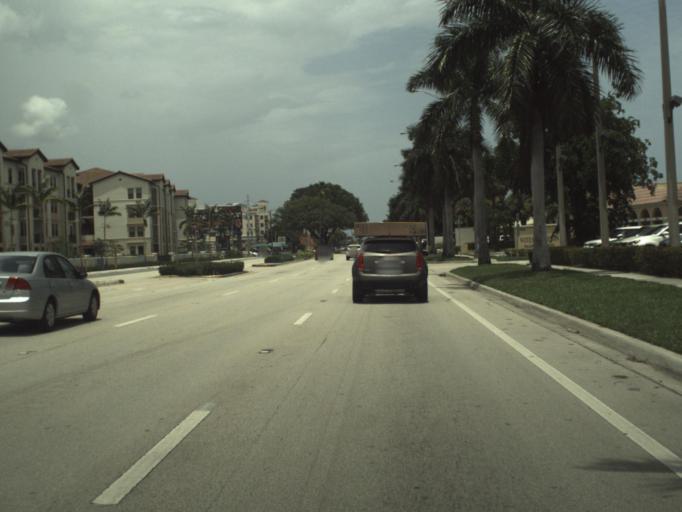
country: US
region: Florida
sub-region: Broward County
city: Pompano Beach Highlands
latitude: 26.2846
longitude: -80.0960
